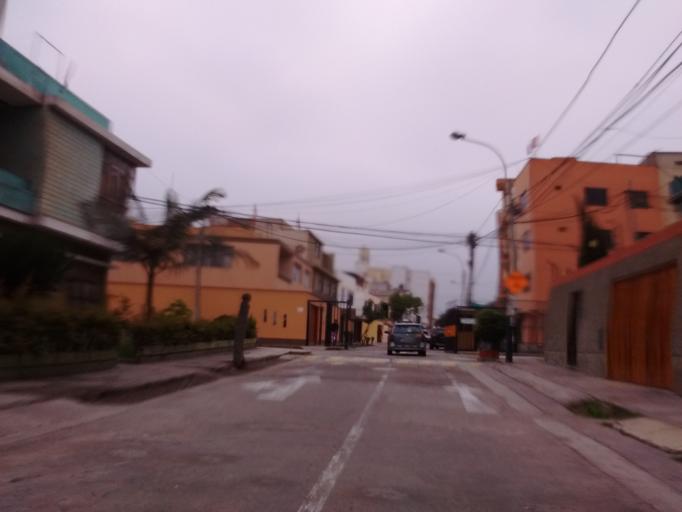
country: PE
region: Callao
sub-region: Callao
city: Callao
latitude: -12.0701
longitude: -77.0721
